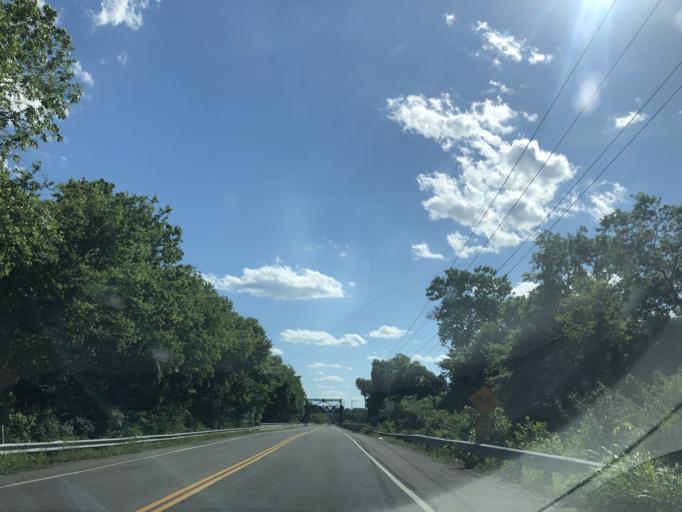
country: US
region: Tennessee
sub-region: Davidson County
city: Belle Meade
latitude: 36.0556
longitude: -86.9267
